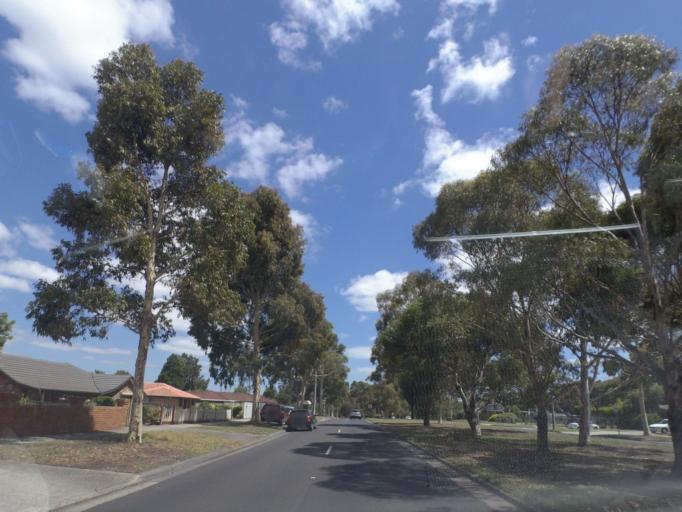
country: AU
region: Victoria
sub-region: Whittlesea
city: Mill Park
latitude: -37.6656
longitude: 145.0582
